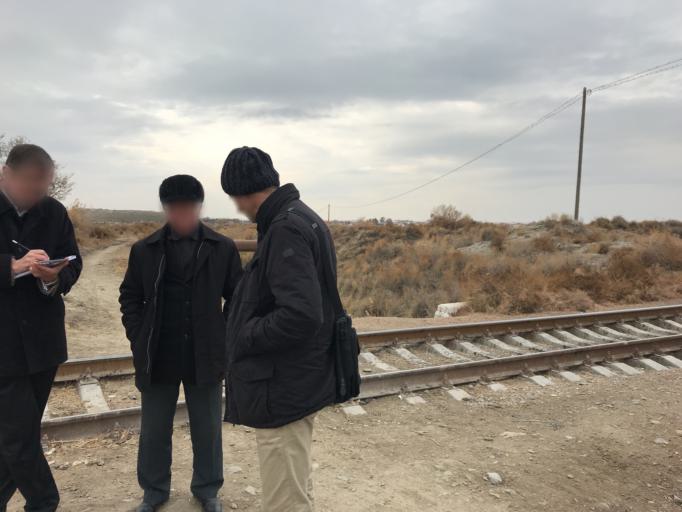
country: UZ
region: Bukhara
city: Kogon
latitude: 39.7170
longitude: 64.5314
